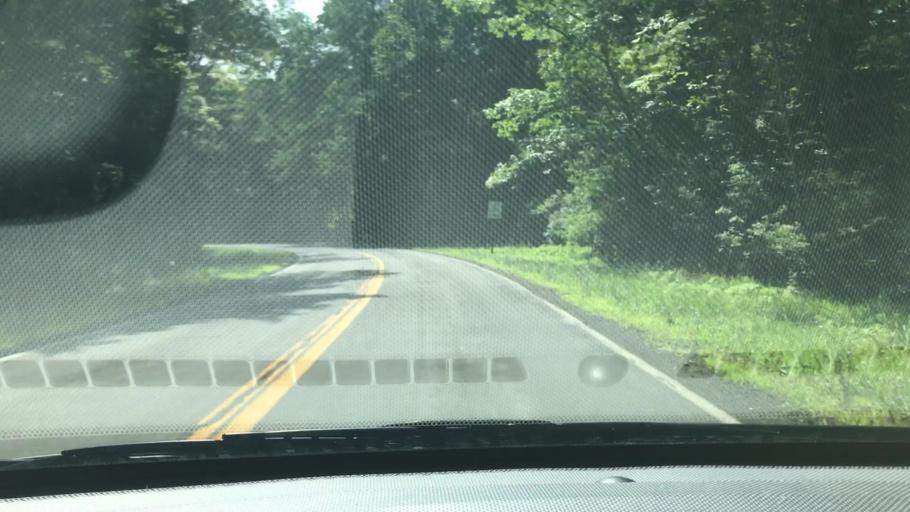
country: US
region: New York
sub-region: Ulster County
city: Shokan
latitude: 41.9302
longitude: -74.2427
